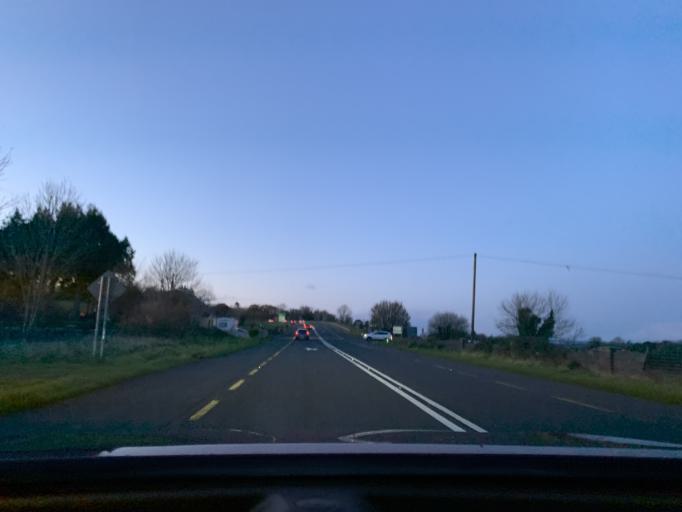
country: IE
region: Connaught
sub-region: Roscommon
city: Boyle
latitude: 53.9674
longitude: -8.2000
